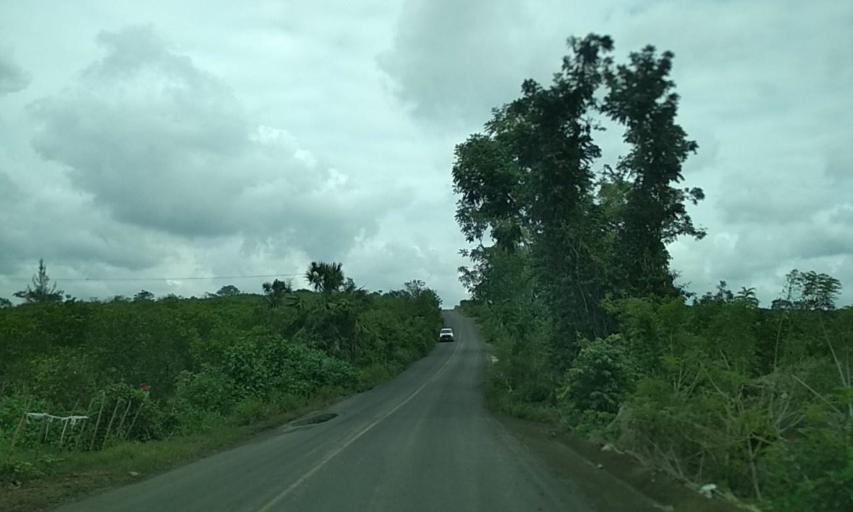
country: MX
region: Veracruz
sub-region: Papantla
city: El Chote
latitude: 20.3480
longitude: -97.3858
